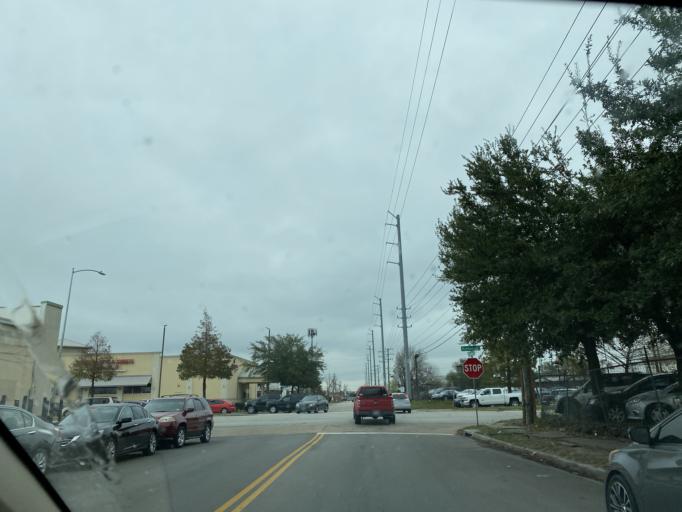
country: US
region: Texas
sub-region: Harris County
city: Piney Point Village
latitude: 29.7287
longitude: -95.5196
